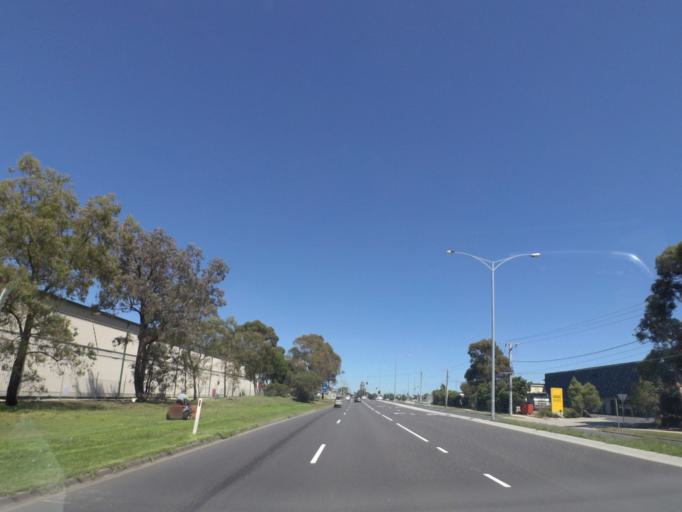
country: AU
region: Victoria
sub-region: Hume
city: Tullamarine
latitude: -37.7073
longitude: 144.8699
